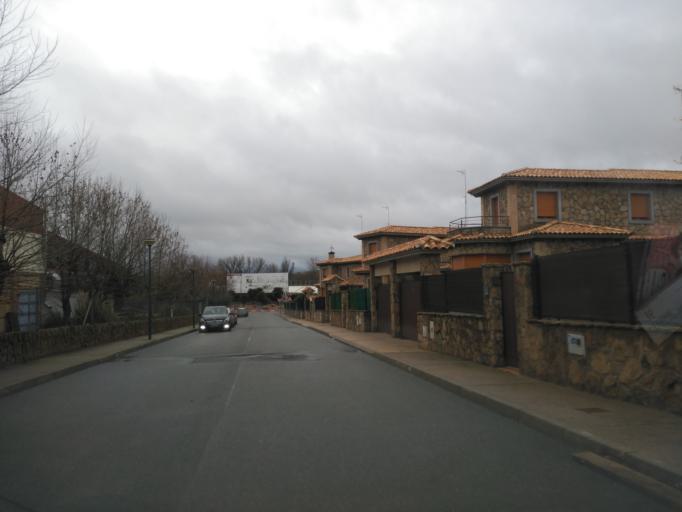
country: ES
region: Castille and Leon
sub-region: Provincia de Salamanca
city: Villamayor
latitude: 40.9846
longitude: -5.7124
